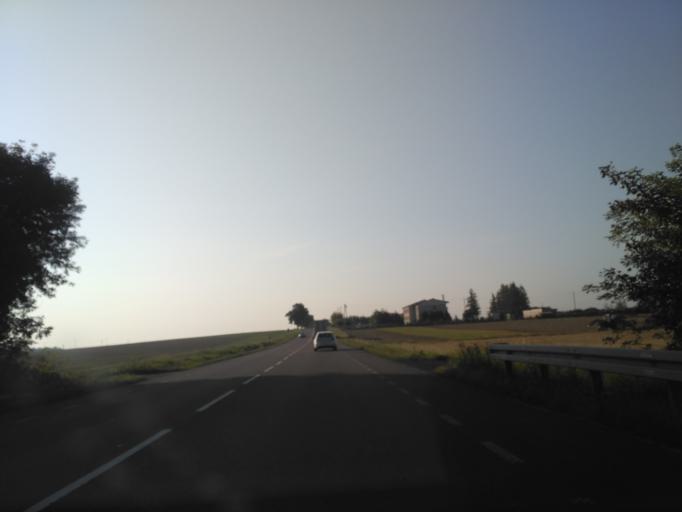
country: PL
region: Lublin Voivodeship
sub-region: Powiat janowski
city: Modliborzyce
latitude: 50.7325
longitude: 22.3573
